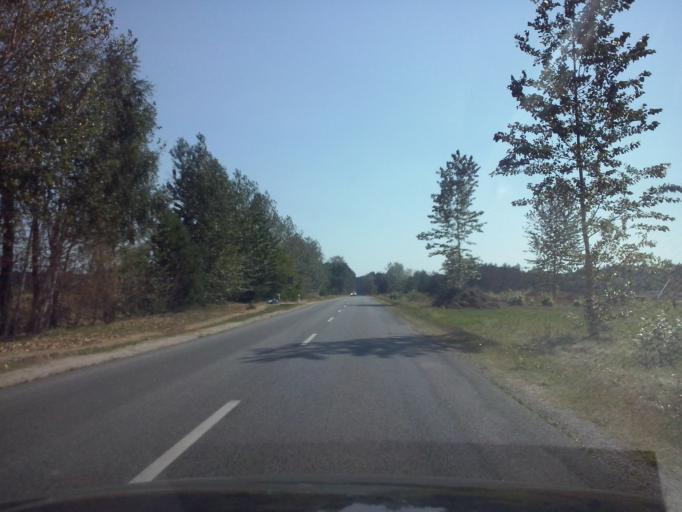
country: PL
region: Swietokrzyskie
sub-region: Powiat kielecki
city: Domaszowice
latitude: 50.8140
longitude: 20.7043
